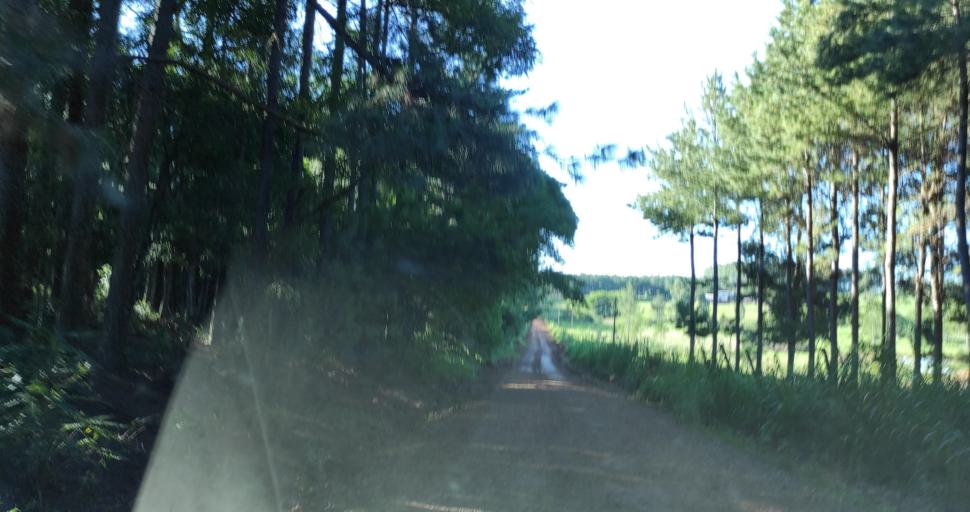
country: AR
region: Misiones
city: Puerto Rico
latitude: -26.8386
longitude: -55.0022
